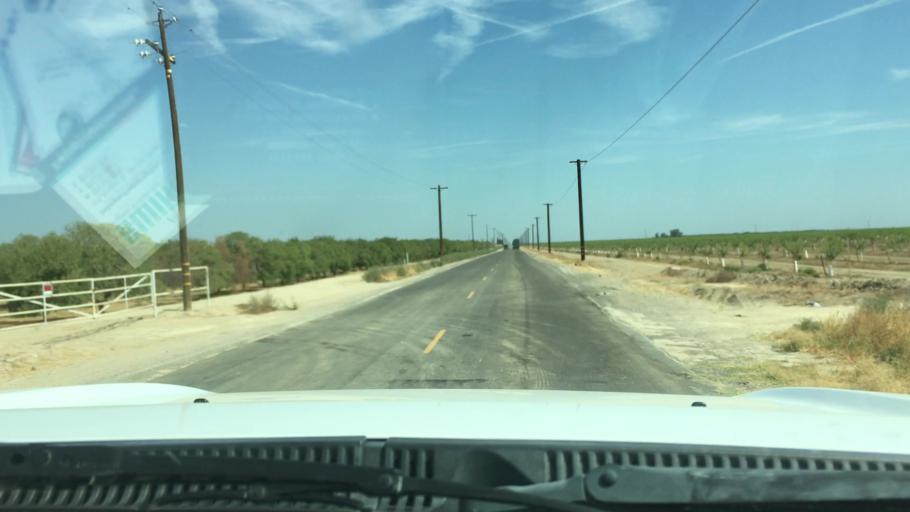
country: US
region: California
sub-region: Kern County
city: Shafter
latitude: 35.4491
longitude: -119.3681
